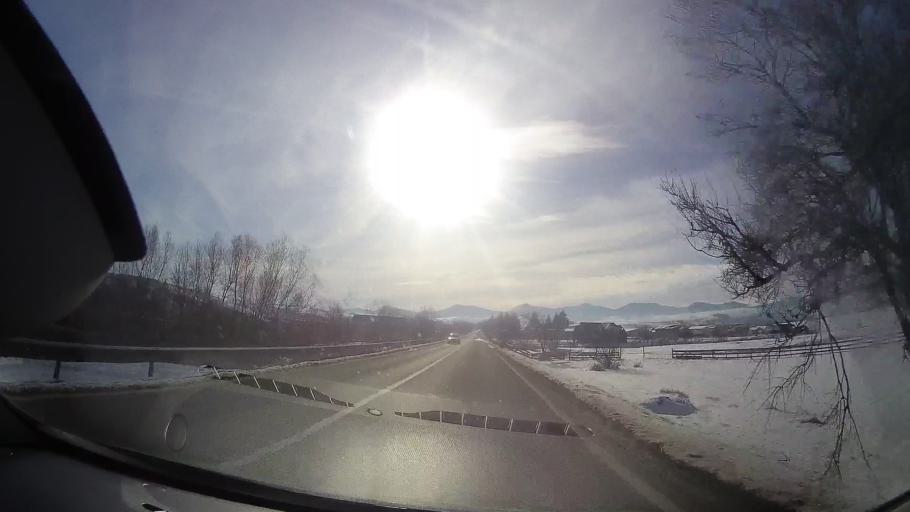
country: RO
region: Neamt
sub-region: Comuna Baltatesti
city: Valea Seaca
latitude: 47.1455
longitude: 26.3202
